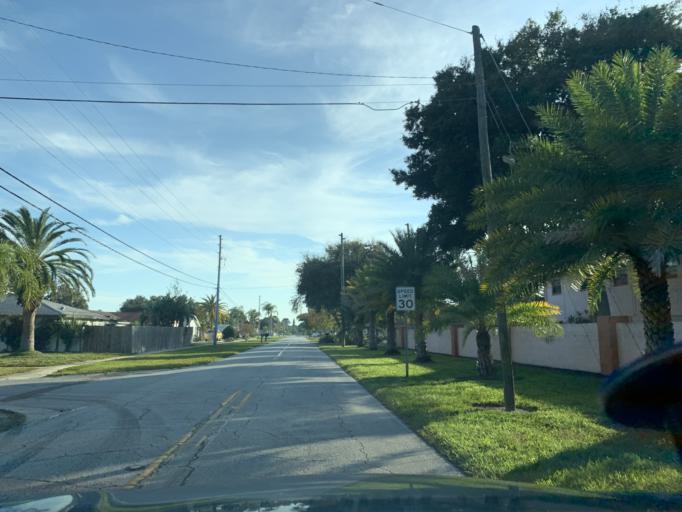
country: US
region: Florida
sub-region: Pinellas County
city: Ridgecrest
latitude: 27.8934
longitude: -82.7974
